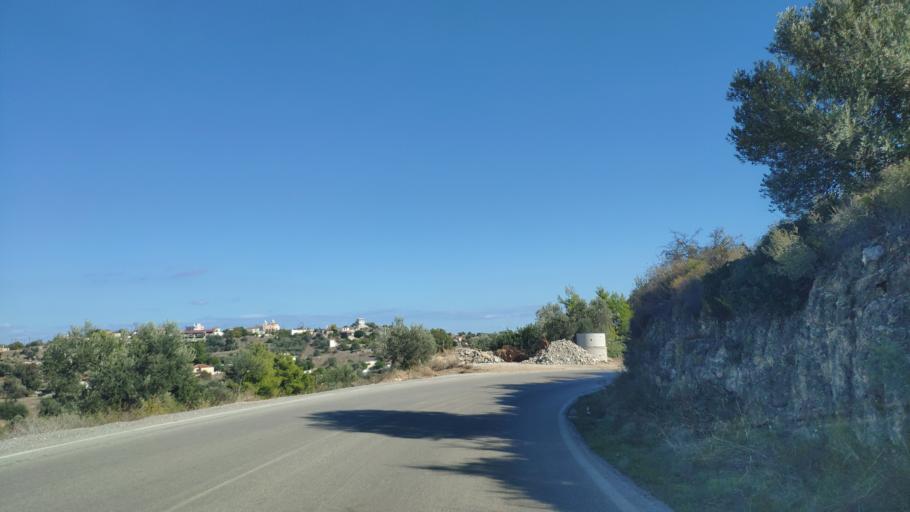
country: GR
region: Attica
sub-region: Nomos Piraios
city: Galatas
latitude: 37.5428
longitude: 23.3656
